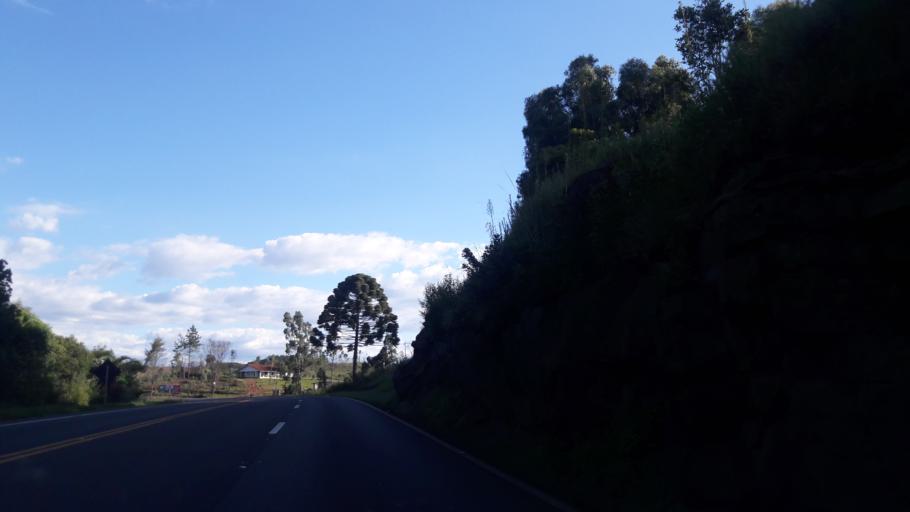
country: BR
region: Parana
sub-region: Guarapuava
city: Guarapuava
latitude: -25.3640
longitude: -51.3496
